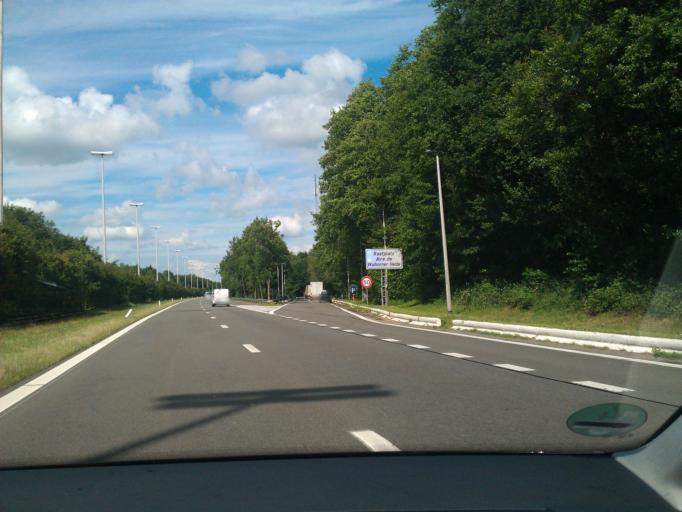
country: BE
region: Wallonia
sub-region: Province de Liege
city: Lontzen
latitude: 50.6861
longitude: 6.0542
